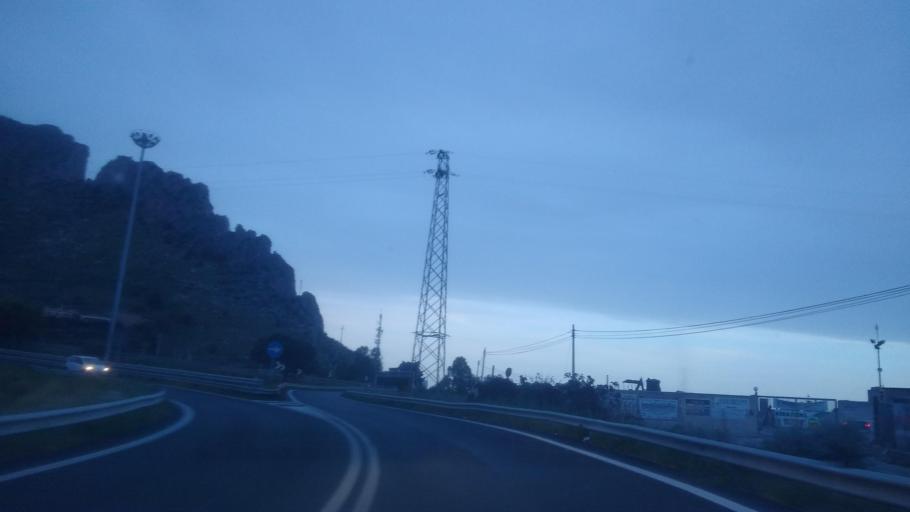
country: IT
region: Sicily
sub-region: Palermo
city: Terrasini
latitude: 38.1372
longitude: 13.0783
